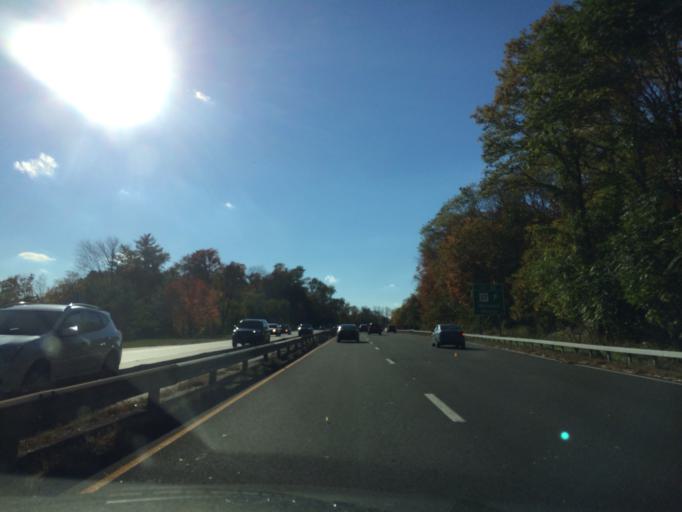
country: US
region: Connecticut
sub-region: Fairfield County
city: Westport
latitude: 41.1646
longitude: -73.3559
